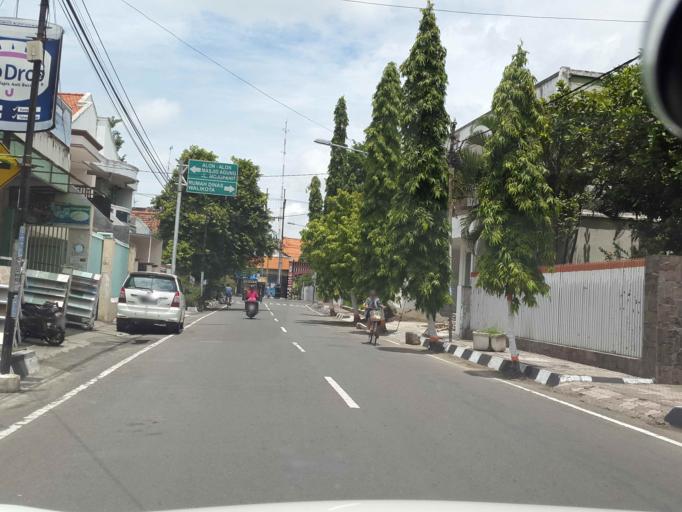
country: ID
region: East Java
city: Mojokerto
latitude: -7.4630
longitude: 112.4364
